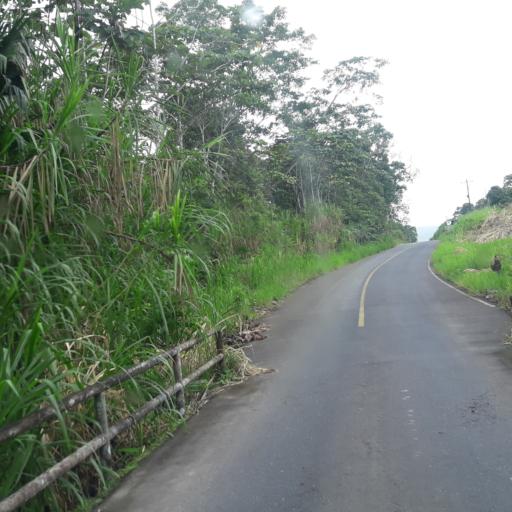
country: EC
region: Napo
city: Tena
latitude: -1.0513
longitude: -77.6636
